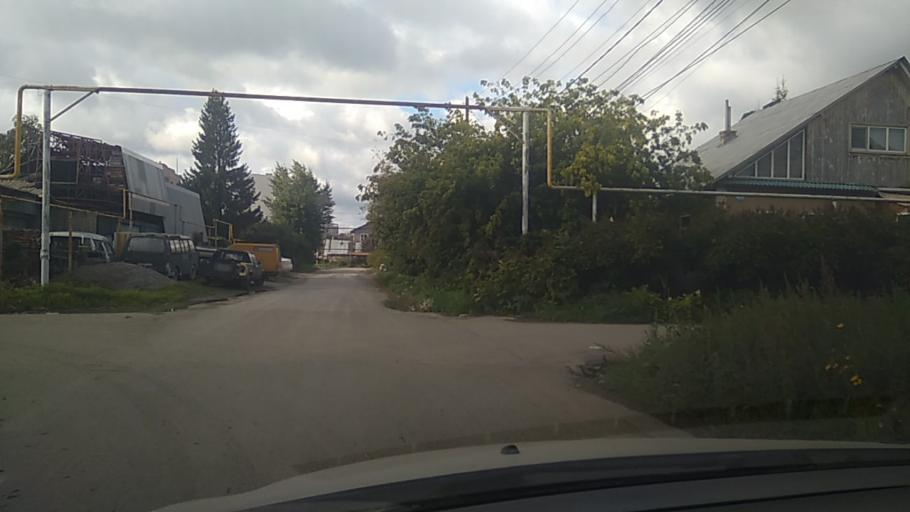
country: RU
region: Sverdlovsk
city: Shirokaya Rechka
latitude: 56.8036
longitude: 60.5029
